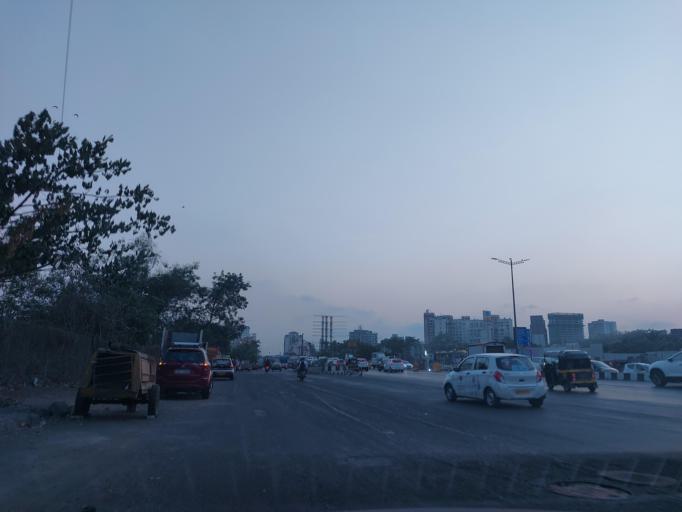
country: IN
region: Maharashtra
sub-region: Mumbai Suburban
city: Mumbai
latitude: 19.0802
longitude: 72.9180
